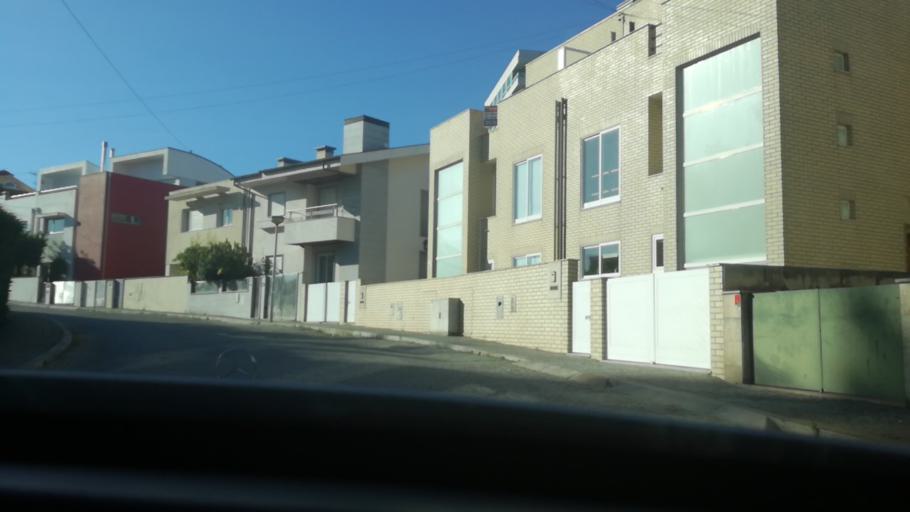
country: PT
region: Porto
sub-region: Maia
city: Maia
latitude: 41.2280
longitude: -8.6111
